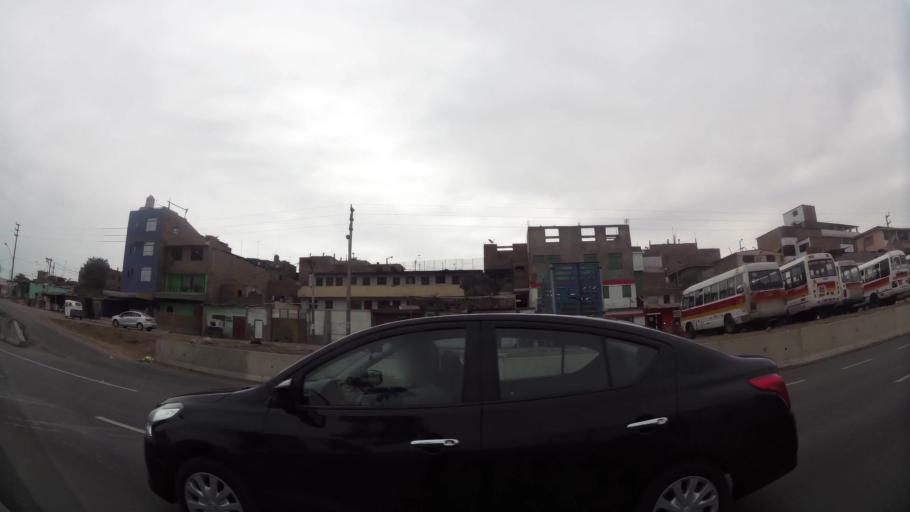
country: PE
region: Lima
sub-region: Lima
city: Surco
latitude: -12.2023
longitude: -76.9743
